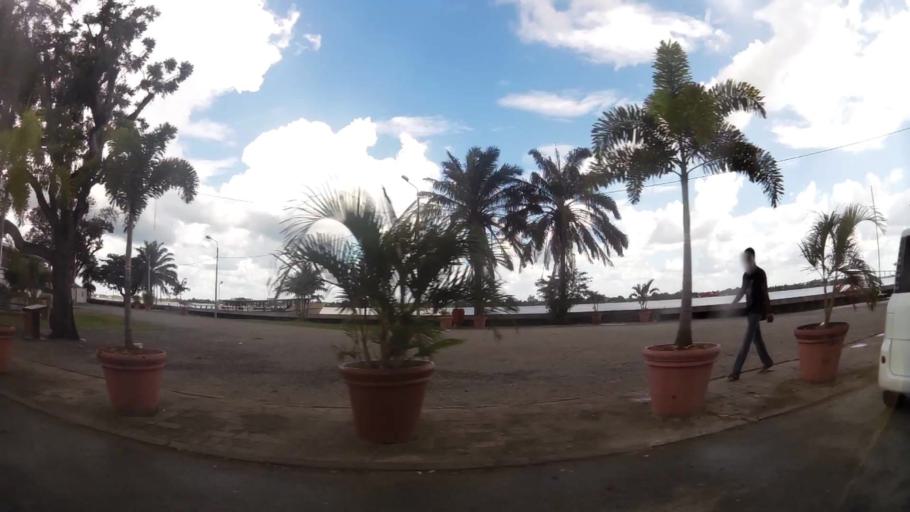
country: SR
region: Paramaribo
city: Paramaribo
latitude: 5.8253
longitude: -55.1517
